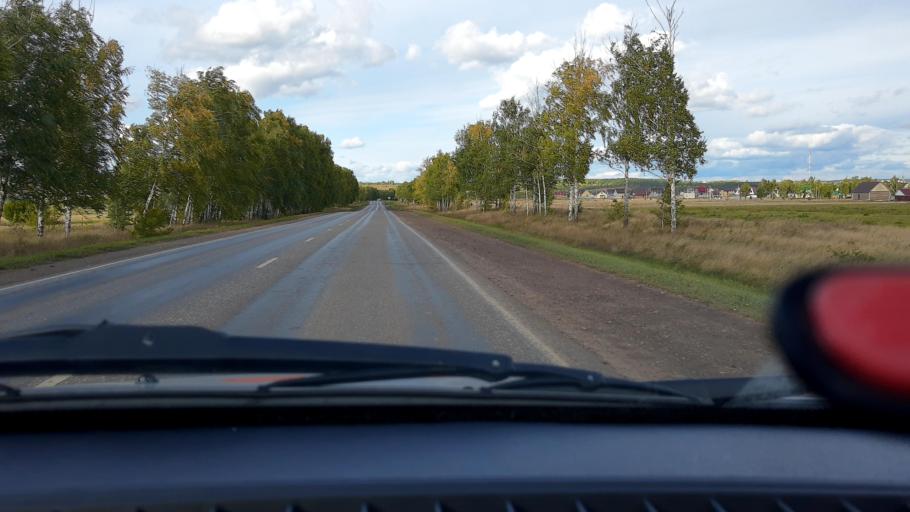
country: RU
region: Bashkortostan
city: Davlekanovo
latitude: 54.2070
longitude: 54.9838
